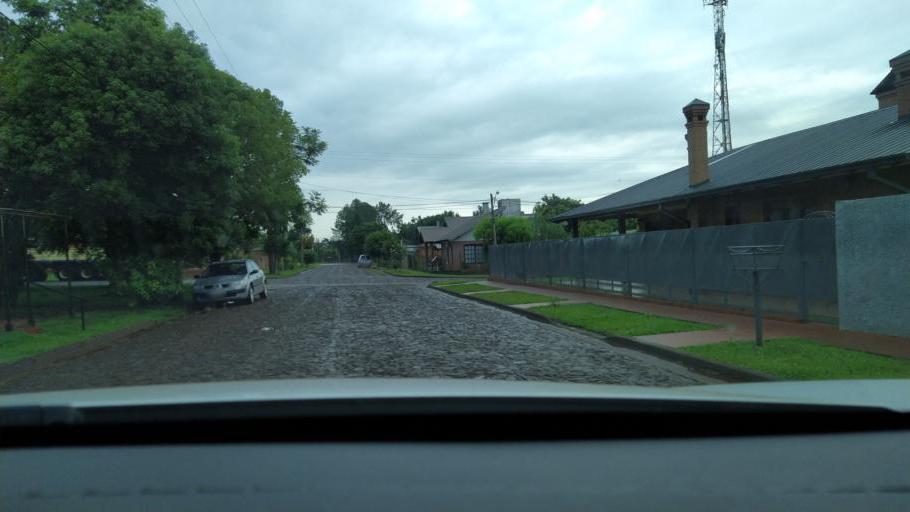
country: AR
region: Misiones
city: Garuhape
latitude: -26.8224
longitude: -54.9555
